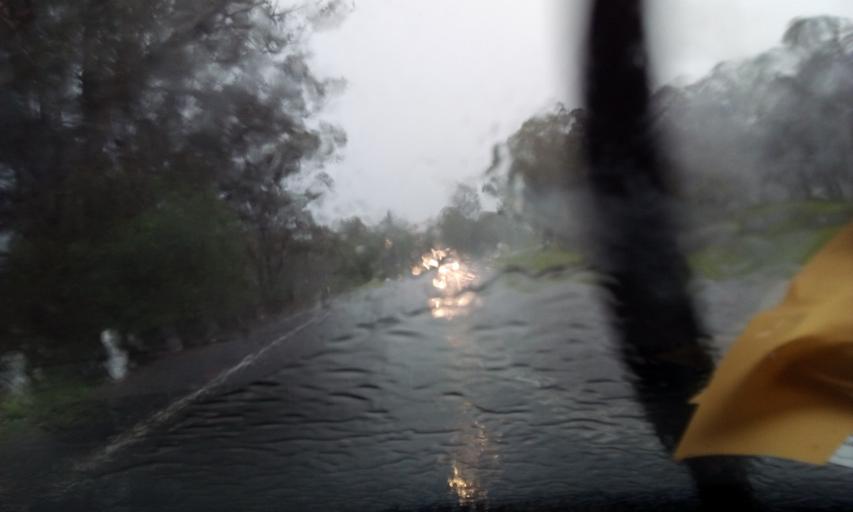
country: AU
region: New South Wales
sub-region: Camden
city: Camden South
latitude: -34.1046
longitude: 150.6983
